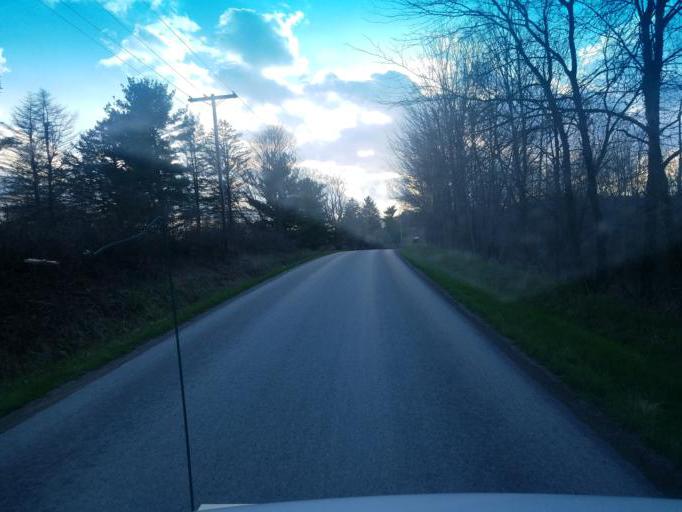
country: US
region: Ohio
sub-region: Morrow County
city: Mount Gilead
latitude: 40.5207
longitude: -82.6931
